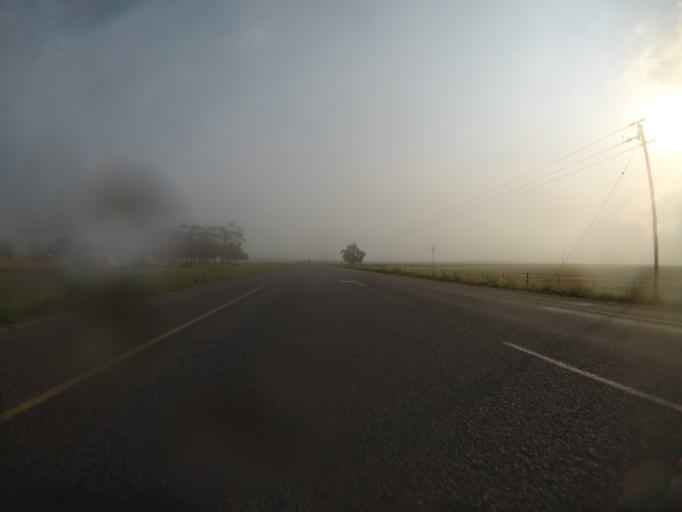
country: ZA
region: Western Cape
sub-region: City of Cape Town
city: Kraaifontein
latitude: -33.6674
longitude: 18.7075
